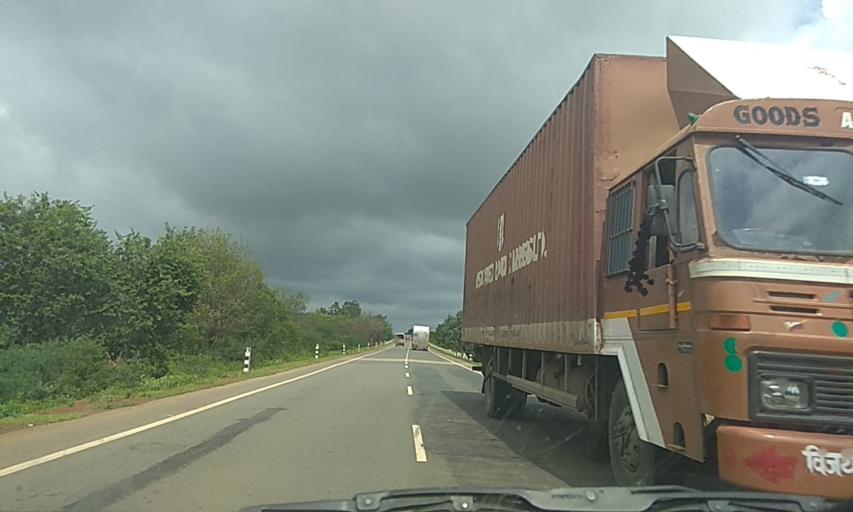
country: IN
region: Karnataka
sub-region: Dharwad
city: Hubli
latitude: 15.3401
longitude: 75.0842
